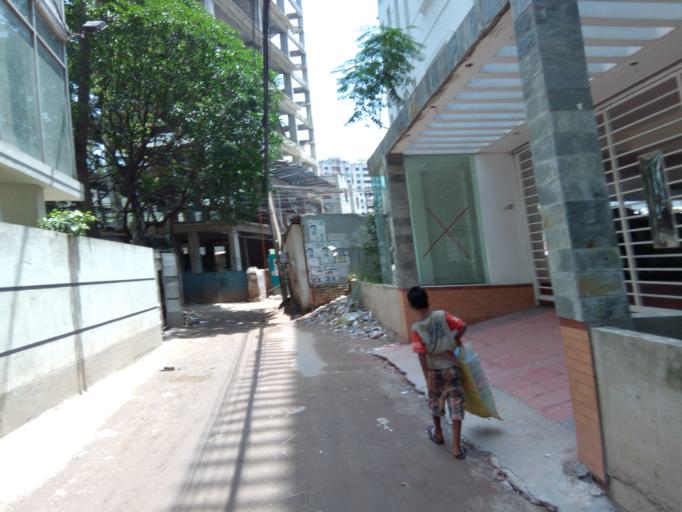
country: BD
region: Dhaka
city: Paltan
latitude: 23.7331
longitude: 90.4106
